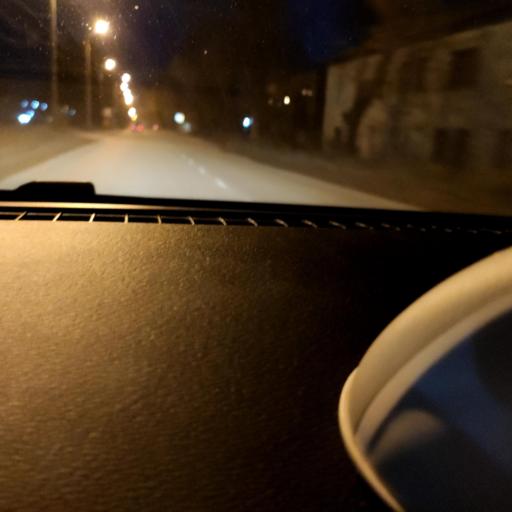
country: RU
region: Samara
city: Petra-Dubrava
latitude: 53.2378
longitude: 50.3076
